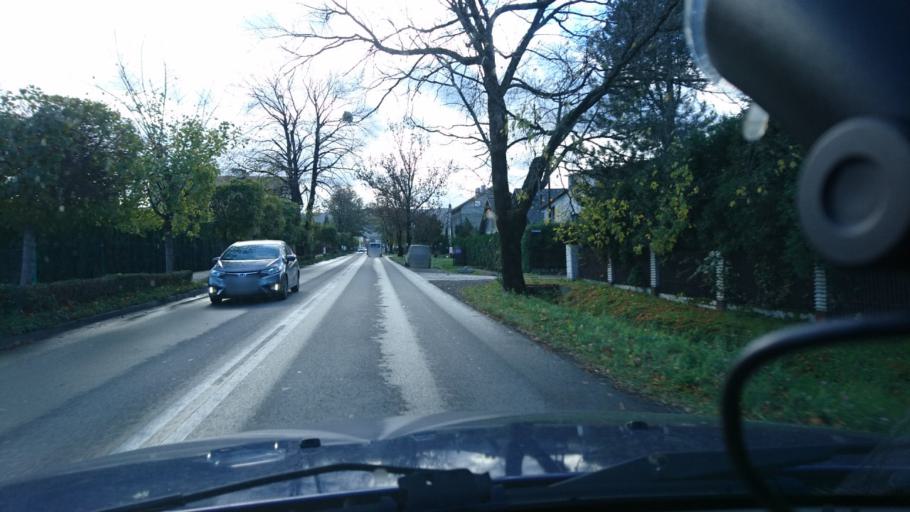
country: PL
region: Silesian Voivodeship
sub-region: Powiat bielski
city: Jasienica
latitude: 49.8081
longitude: 18.9211
